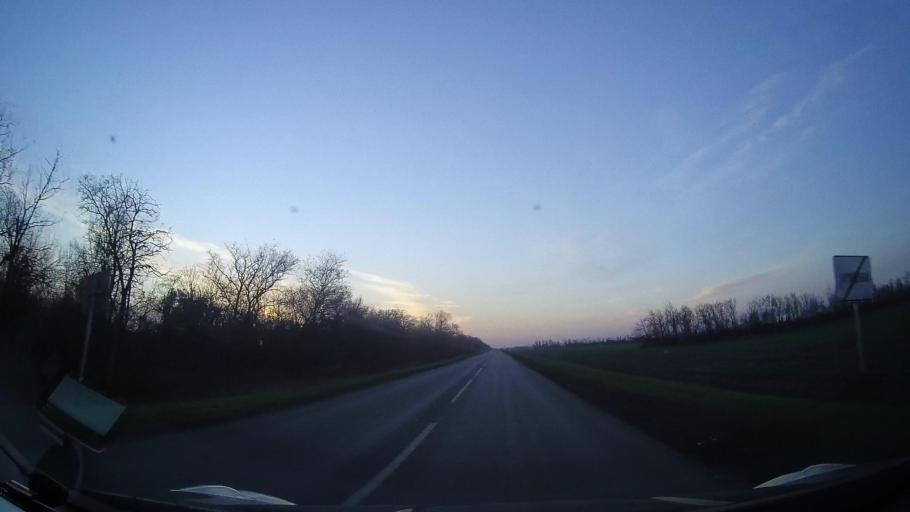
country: RU
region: Rostov
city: Zernograd
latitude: 46.9251
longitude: 40.3597
